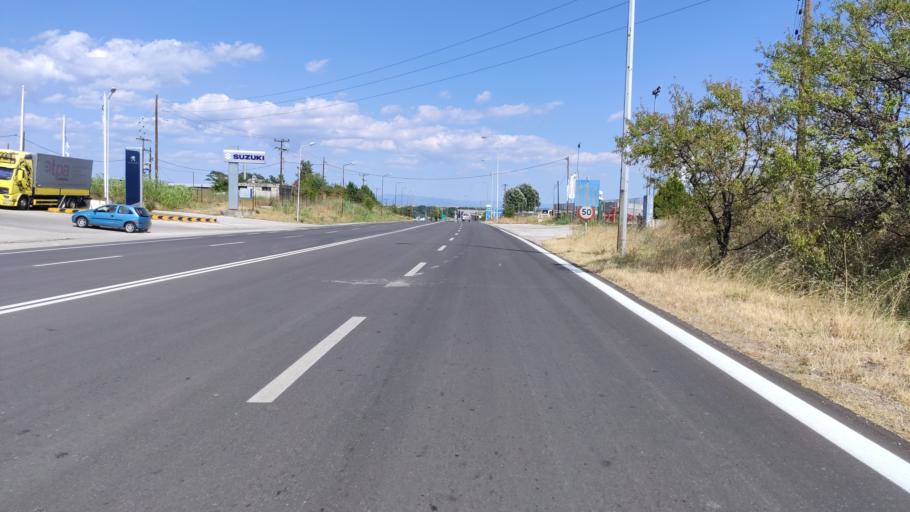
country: GR
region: East Macedonia and Thrace
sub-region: Nomos Rodopis
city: Komotini
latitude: 41.1084
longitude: 25.3544
